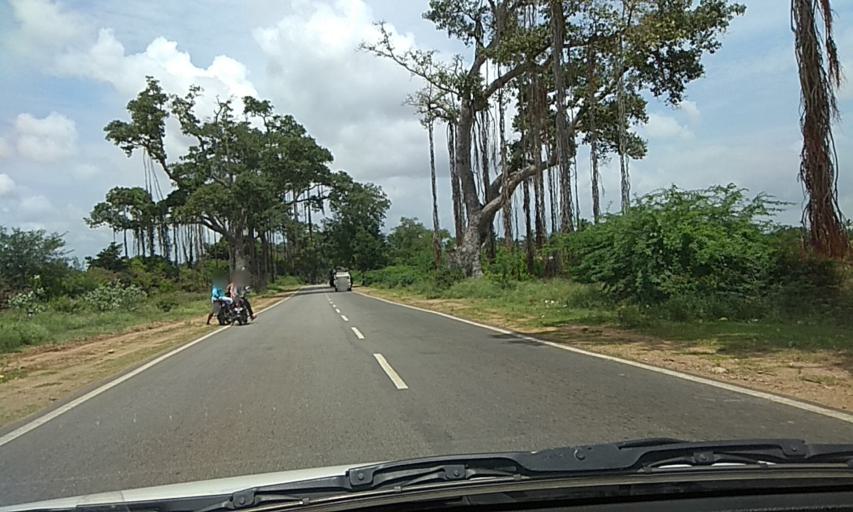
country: IN
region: Karnataka
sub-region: Chamrajnagar
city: Gundlupet
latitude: 11.8109
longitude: 76.7127
